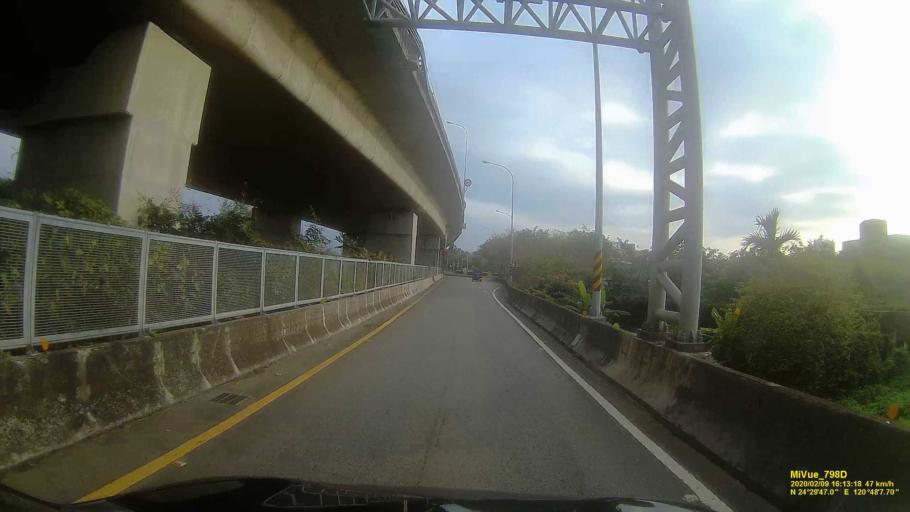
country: TW
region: Taiwan
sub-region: Miaoli
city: Miaoli
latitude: 24.4963
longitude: 120.8021
